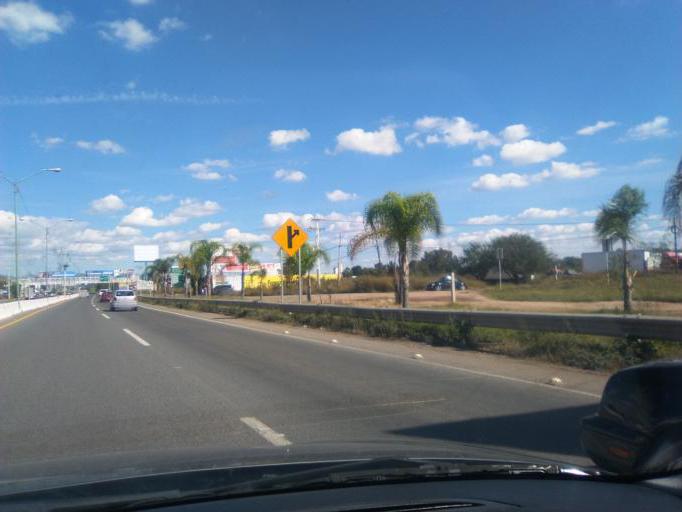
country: MX
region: Guanajuato
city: Silao
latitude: 20.9457
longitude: -101.4129
